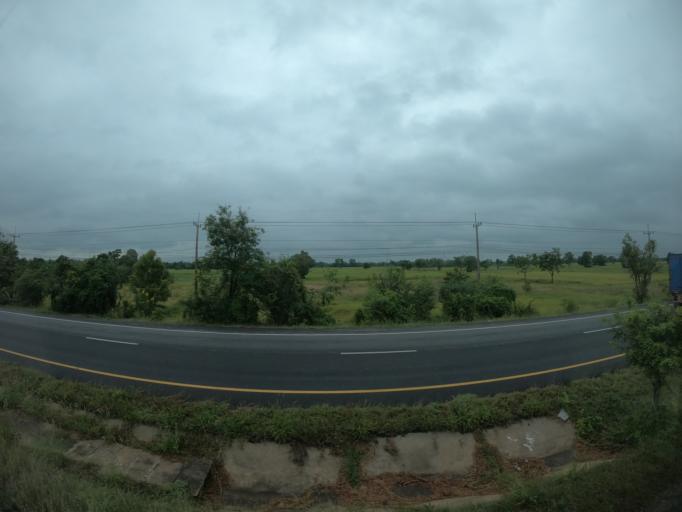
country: TH
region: Nakhon Ratchasima
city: Sida
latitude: 15.5934
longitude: 102.5593
